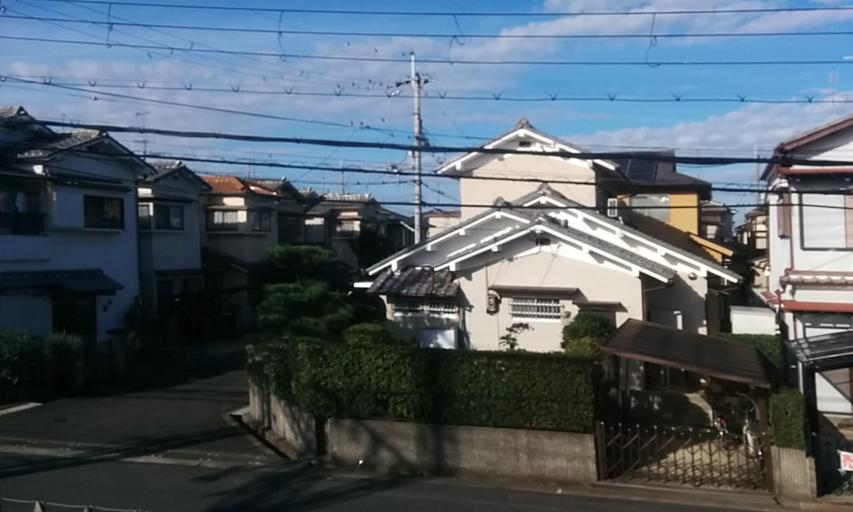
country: JP
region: Kyoto
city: Tanabe
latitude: 34.8483
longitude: 135.7719
